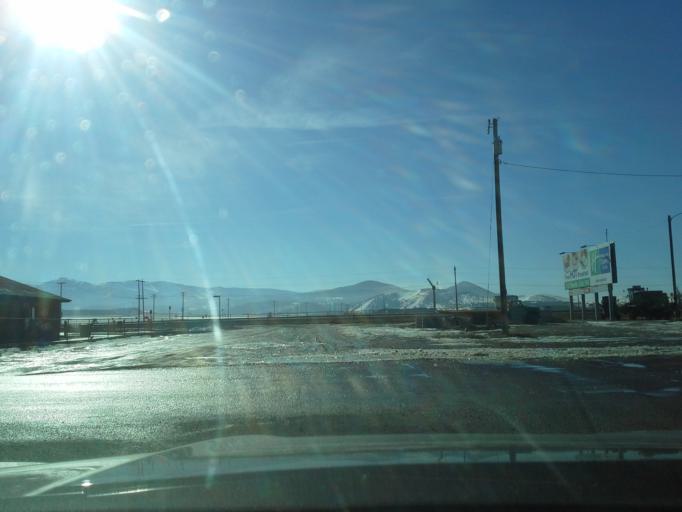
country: US
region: Montana
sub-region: Lewis and Clark County
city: East Helena
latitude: 46.5878
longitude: -111.9110
